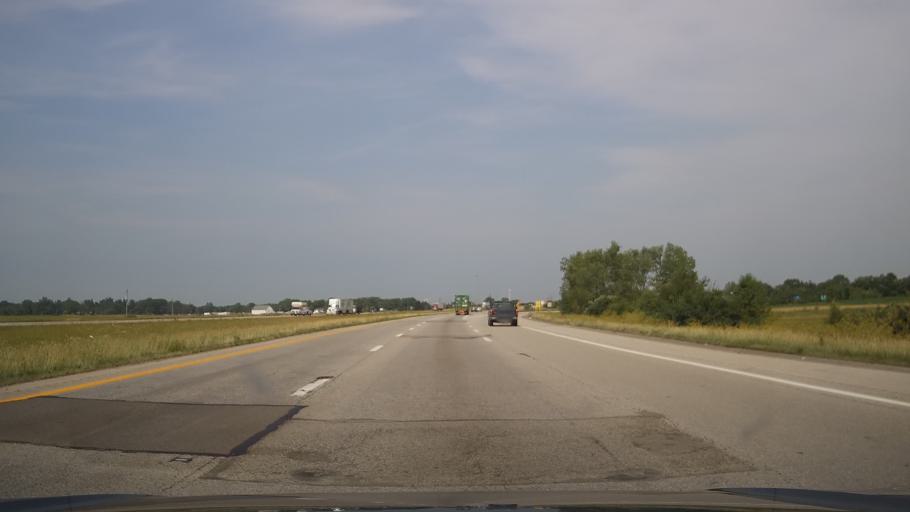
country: US
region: Ohio
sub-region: Franklin County
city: Grove City
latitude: 39.8252
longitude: -83.1322
